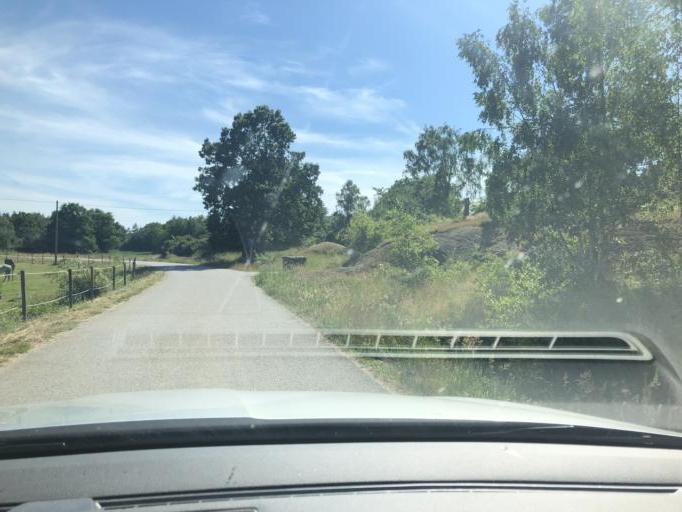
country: SE
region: Blekinge
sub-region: Karlshamns Kommun
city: Morrum
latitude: 56.1600
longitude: 14.8008
